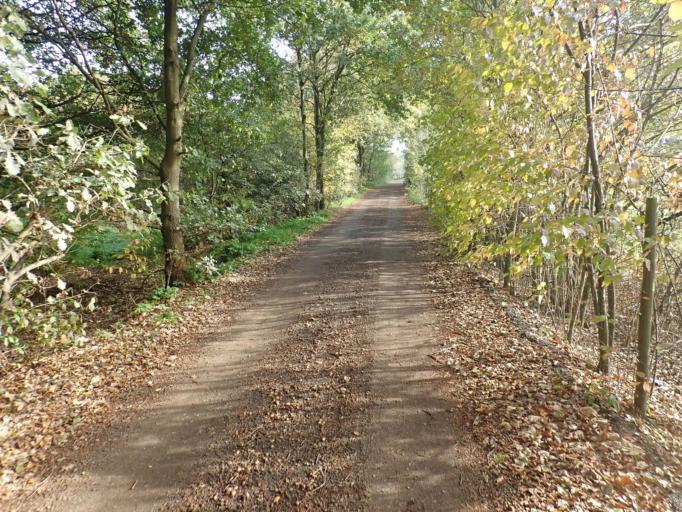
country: BE
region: Flanders
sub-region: Provincie Antwerpen
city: Ranst
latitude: 51.2100
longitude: 4.5549
